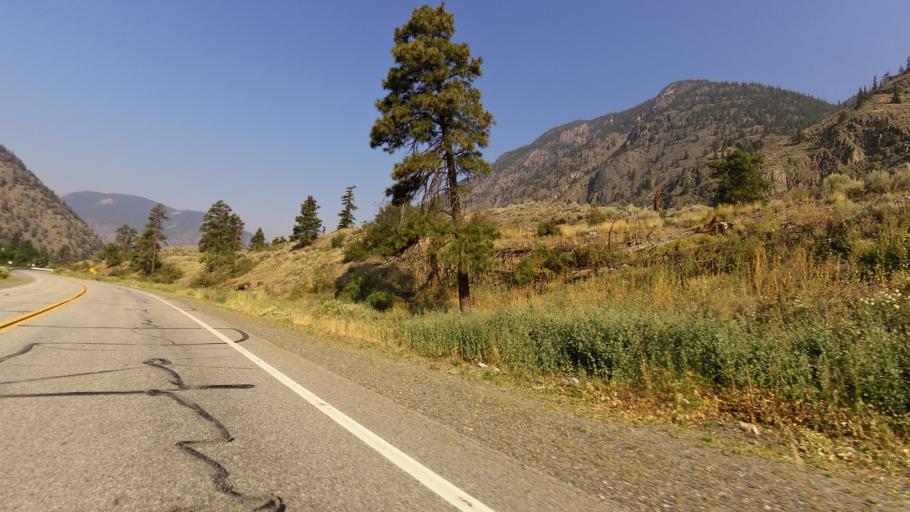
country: CA
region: British Columbia
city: Oliver
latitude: 49.2183
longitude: -119.9234
